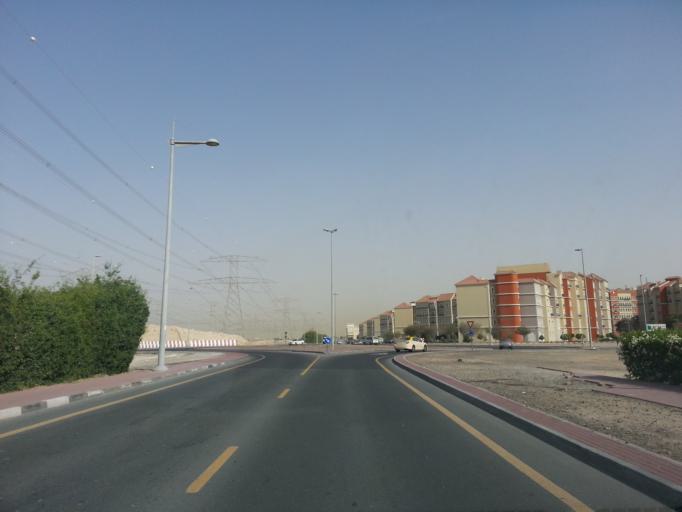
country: AE
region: Dubai
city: Dubai
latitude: 25.0409
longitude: 55.1465
